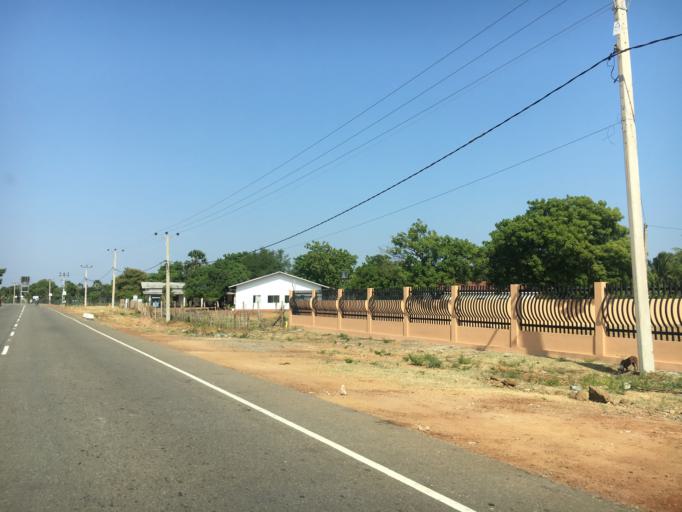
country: LK
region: Northern Province
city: Kilinochchi
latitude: 9.4372
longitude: 80.4040
